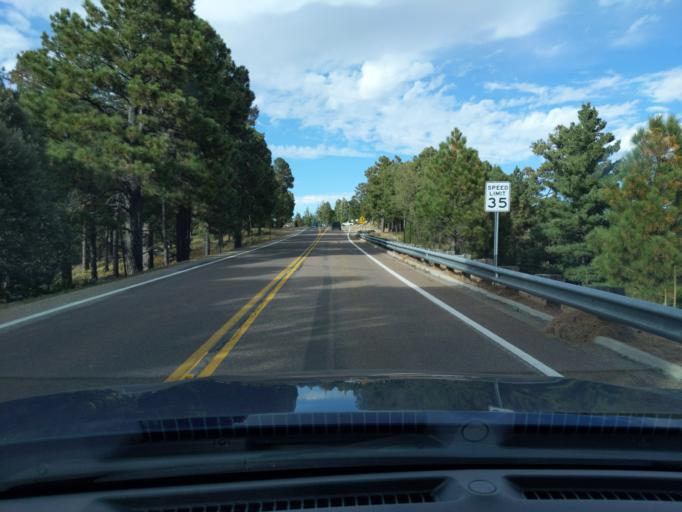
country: US
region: Arizona
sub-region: Pinal County
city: Oracle
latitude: 32.4379
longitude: -110.7524
